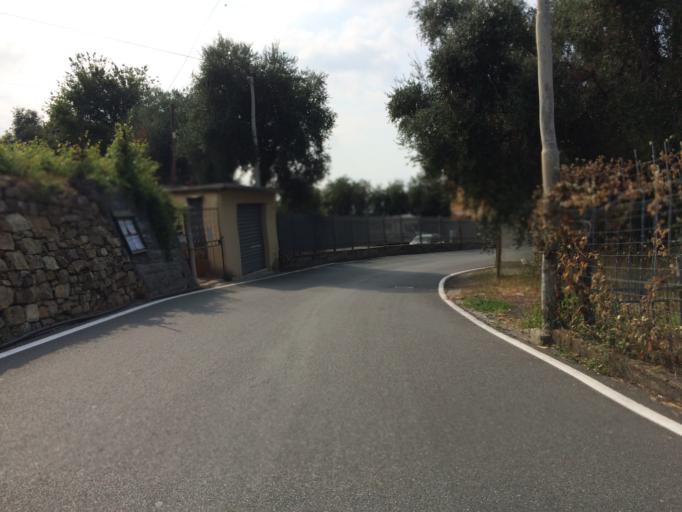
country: IT
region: Liguria
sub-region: Provincia di Imperia
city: San Remo
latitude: 43.8298
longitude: 7.7637
